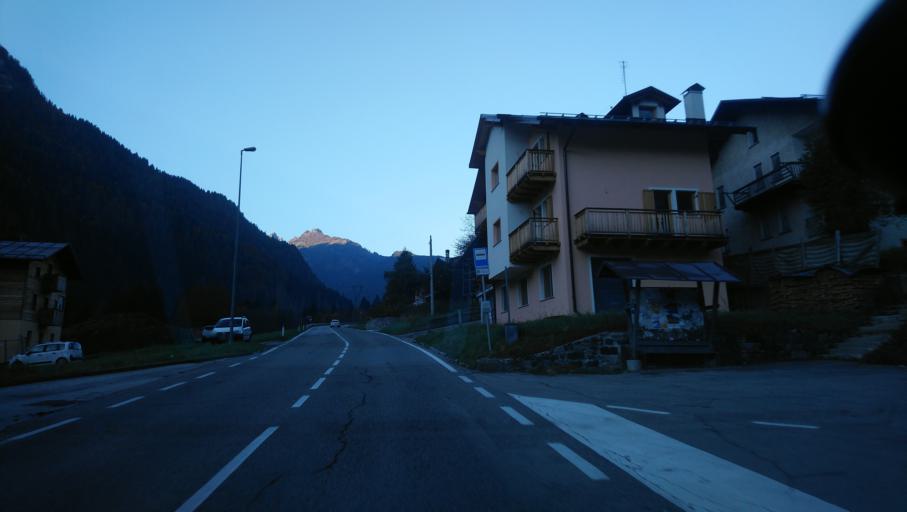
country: IT
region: Veneto
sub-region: Provincia di Belluno
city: Vallada Agordina
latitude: 46.3641
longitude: 11.9417
